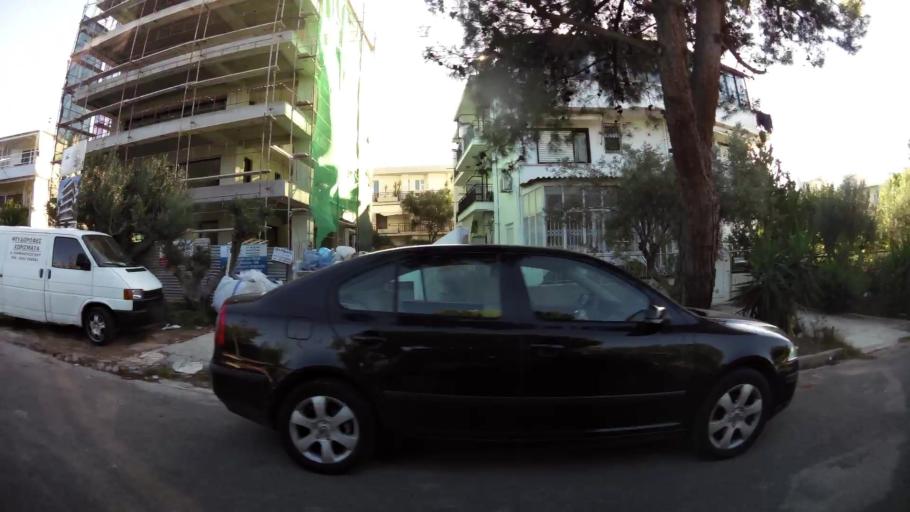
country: GR
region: Attica
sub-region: Nomarchia Athinas
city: Glyfada
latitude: 37.8766
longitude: 23.7494
